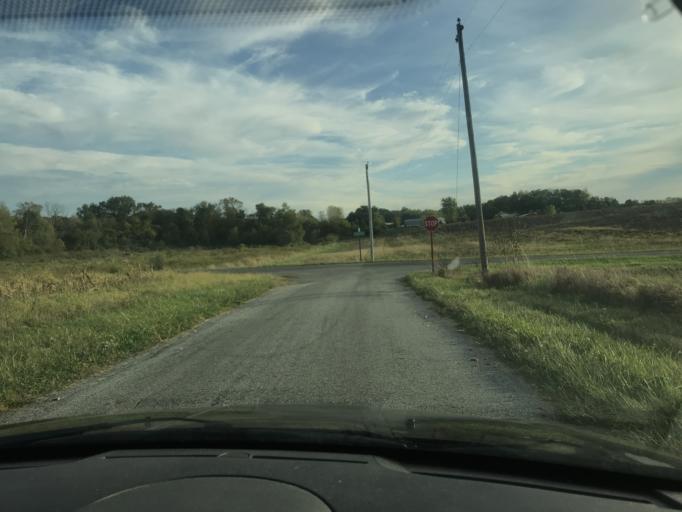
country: US
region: Ohio
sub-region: Logan County
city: West Liberty
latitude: 40.1958
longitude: -83.8077
